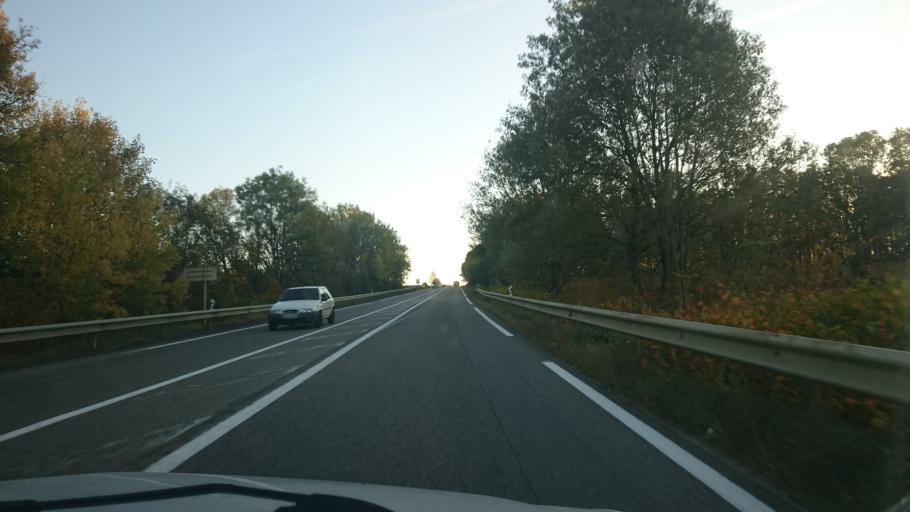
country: FR
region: Franche-Comte
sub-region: Departement du Doubs
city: Quingey
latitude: 47.0581
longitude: 5.8819
